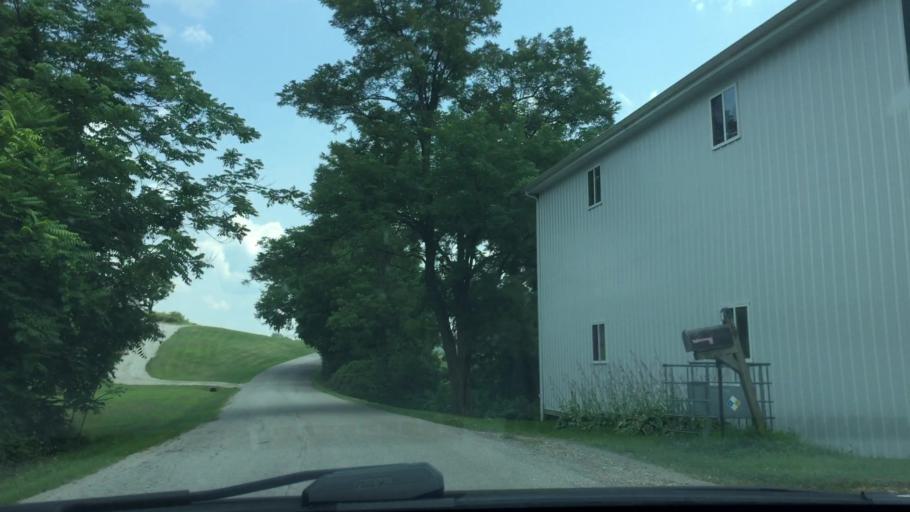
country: US
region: West Virginia
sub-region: Wetzel County
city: New Martinsville
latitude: 39.7116
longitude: -80.7483
